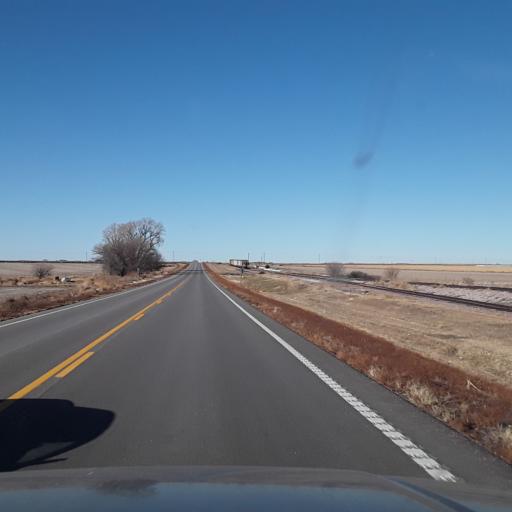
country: US
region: Nebraska
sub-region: Phelps County
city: Holdrege
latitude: 40.4855
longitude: -99.5240
